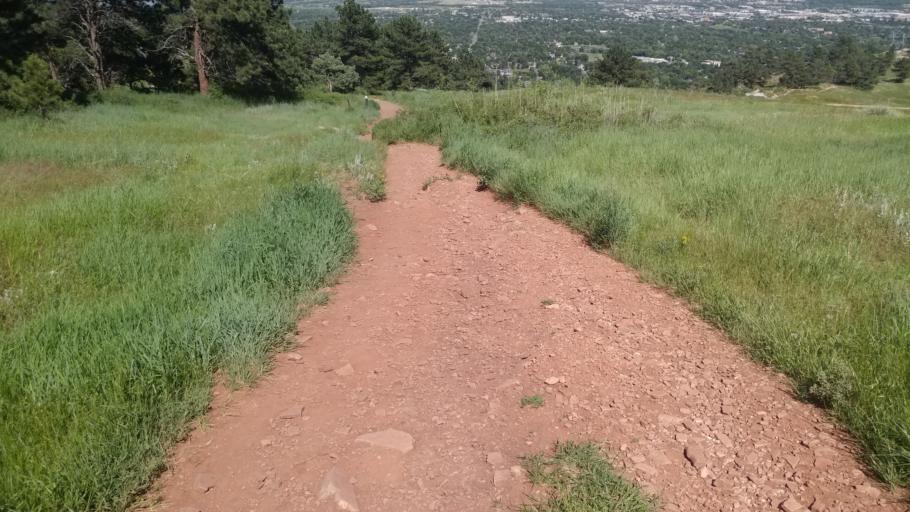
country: US
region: Colorado
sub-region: Boulder County
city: Boulder
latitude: 40.0357
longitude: -105.2997
